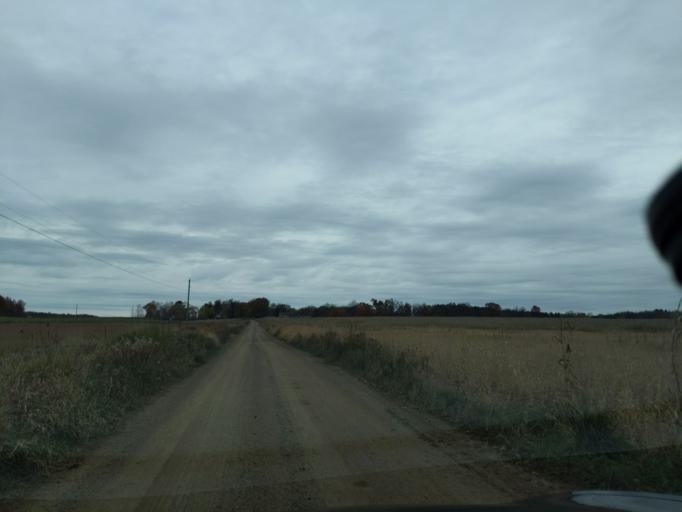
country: US
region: Michigan
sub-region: Eaton County
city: Eaton Rapids
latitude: 42.4245
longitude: -84.6004
